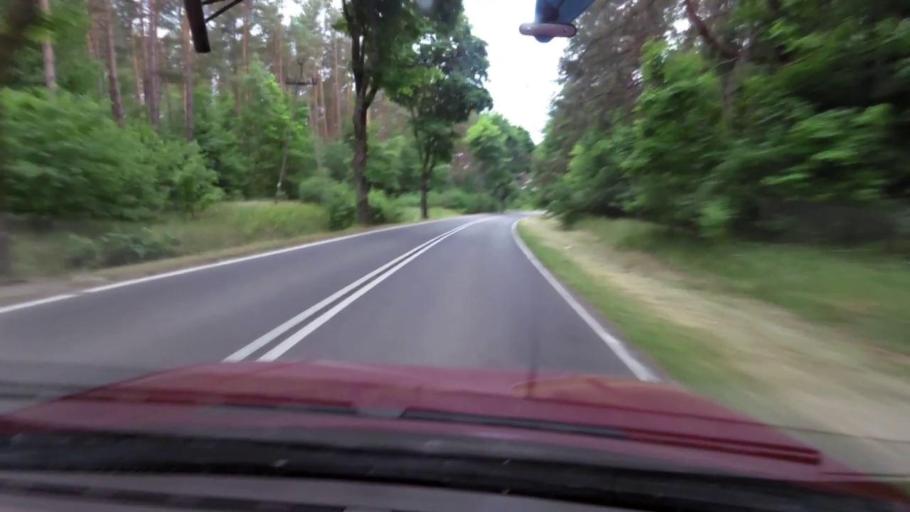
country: PL
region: West Pomeranian Voivodeship
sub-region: Powiat koszalinski
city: Sianow
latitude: 54.1814
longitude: 16.3300
